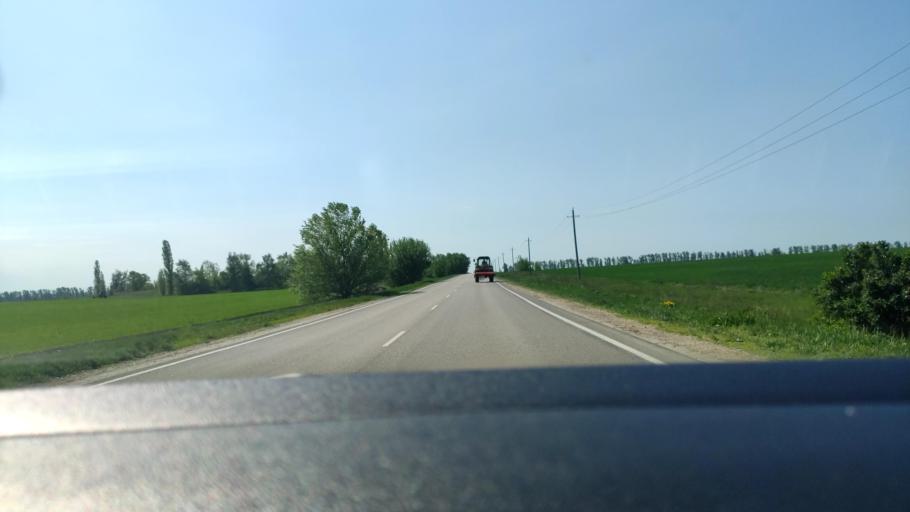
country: RU
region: Voronezj
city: Novaya Usman'
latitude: 51.5756
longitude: 39.3752
